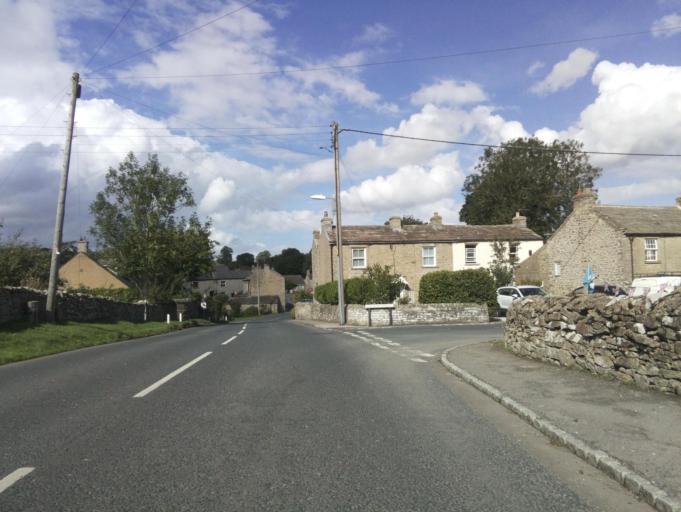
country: GB
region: England
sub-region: North Yorkshire
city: Leyburn
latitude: 54.3304
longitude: -1.8253
